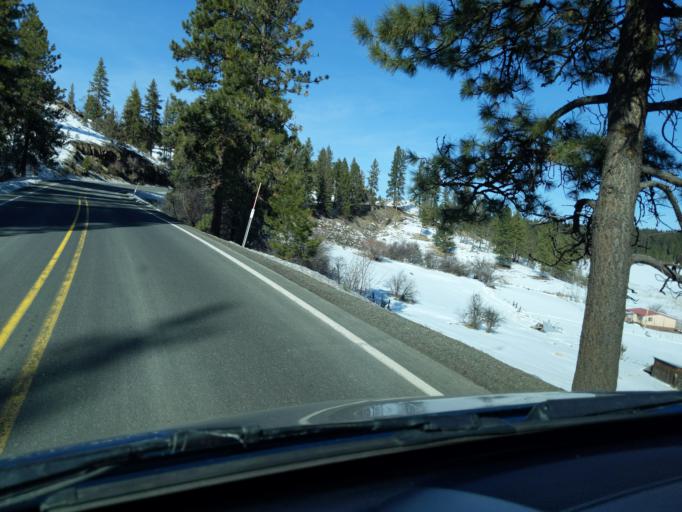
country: US
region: Oregon
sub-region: Grant County
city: John Day
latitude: 44.9057
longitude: -119.0111
